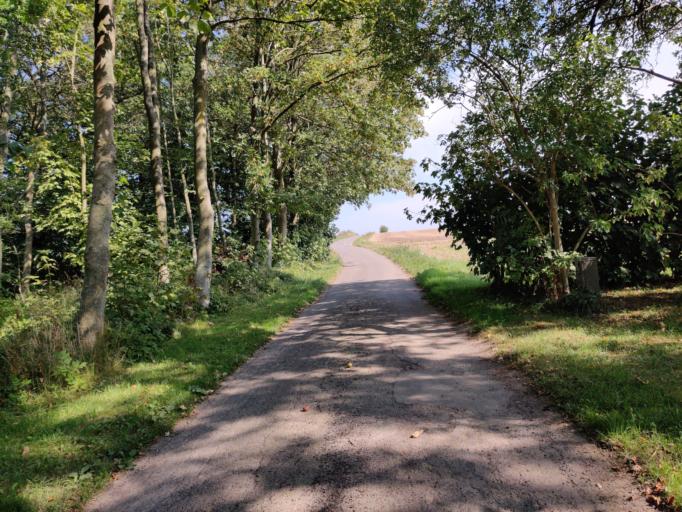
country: DK
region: Zealand
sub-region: Guldborgsund Kommune
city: Nykobing Falster
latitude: 54.6819
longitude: 11.8849
